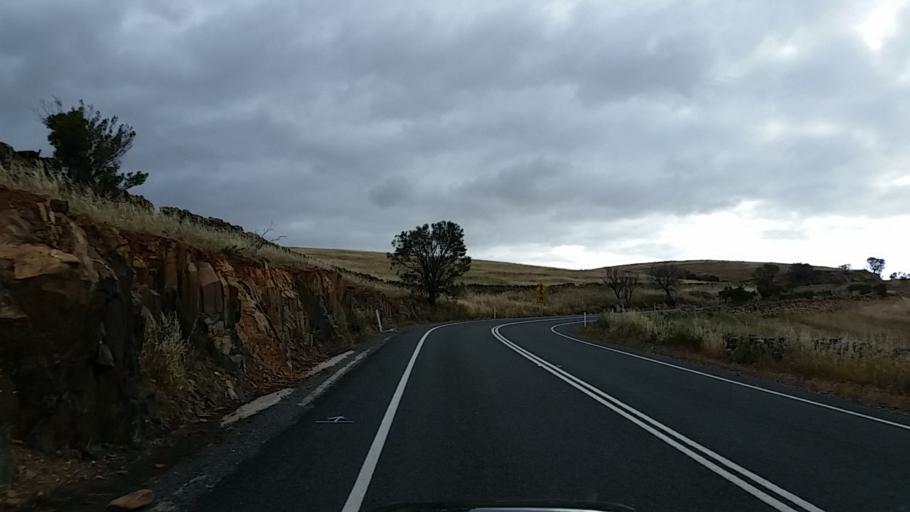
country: AU
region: South Australia
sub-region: Barossa
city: Angaston
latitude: -34.5621
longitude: 139.2166
